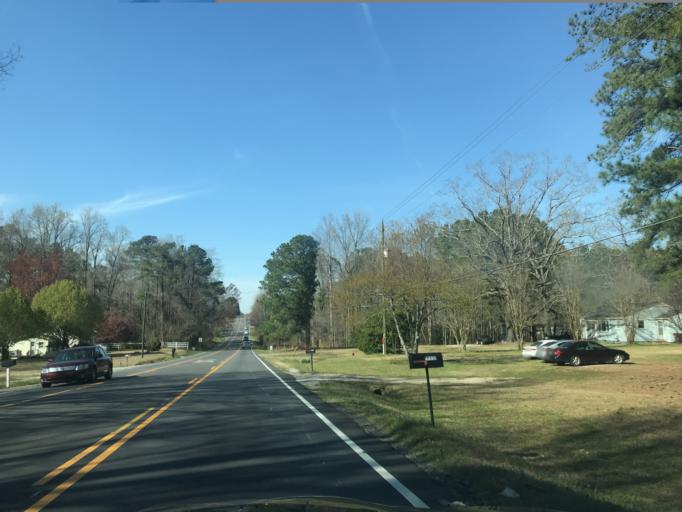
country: US
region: North Carolina
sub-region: Wake County
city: Fuquay-Varina
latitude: 35.5652
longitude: -78.7550
